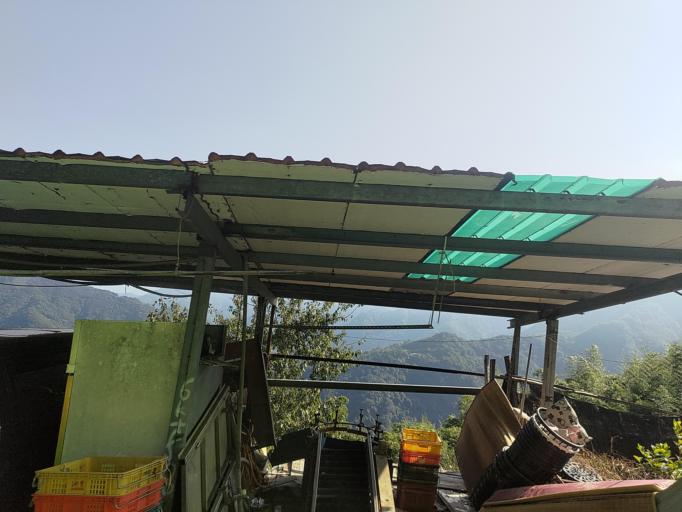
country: TW
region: Taiwan
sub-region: Hsinchu
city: Hsinchu
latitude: 24.6113
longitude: 121.0982
